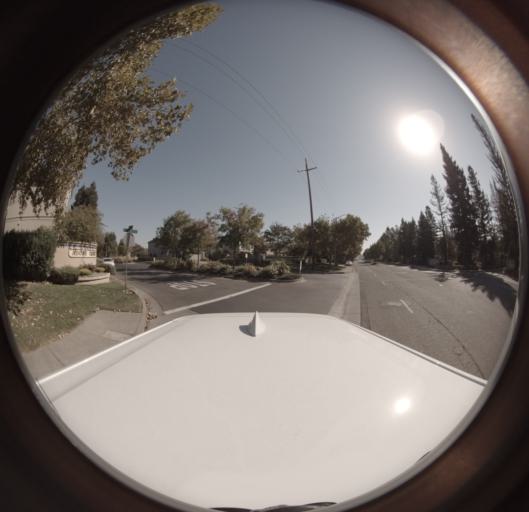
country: US
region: California
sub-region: Sonoma County
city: Petaluma
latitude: 38.2410
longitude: -122.5911
